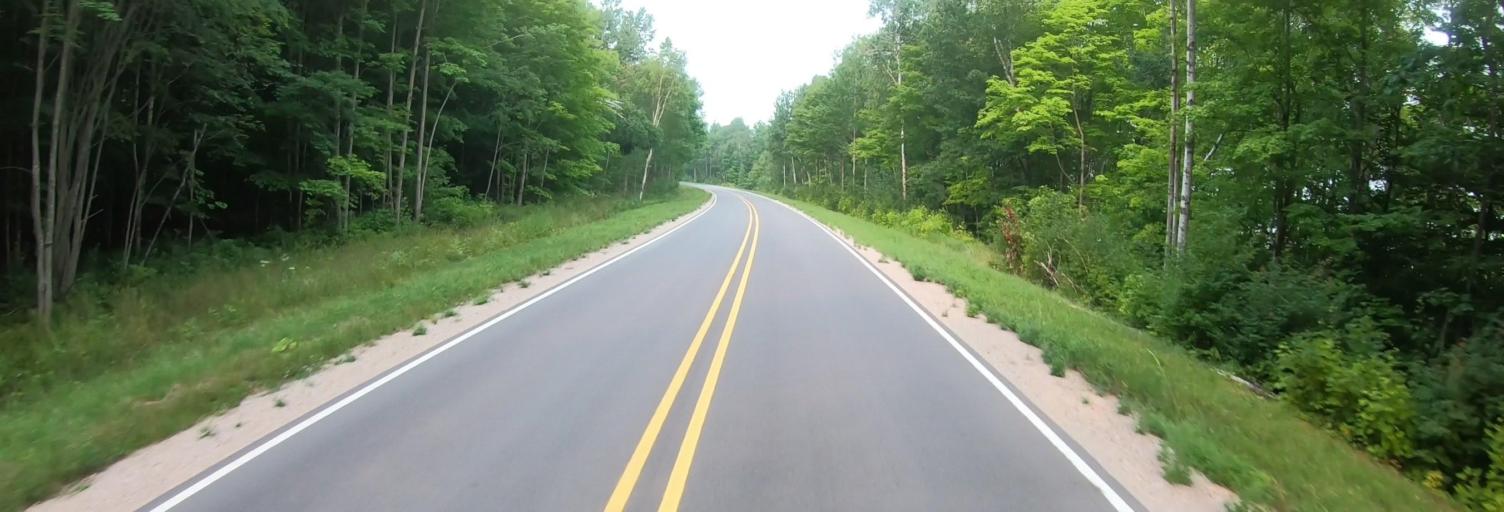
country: US
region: Michigan
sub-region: Luce County
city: Newberry
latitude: 46.4762
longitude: -84.9493
